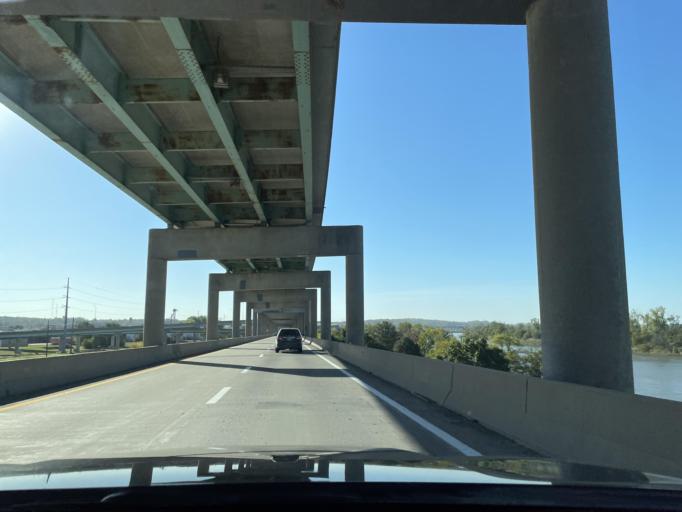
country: US
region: Missouri
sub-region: Buchanan County
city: Saint Joseph
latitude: 39.7666
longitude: -94.8607
